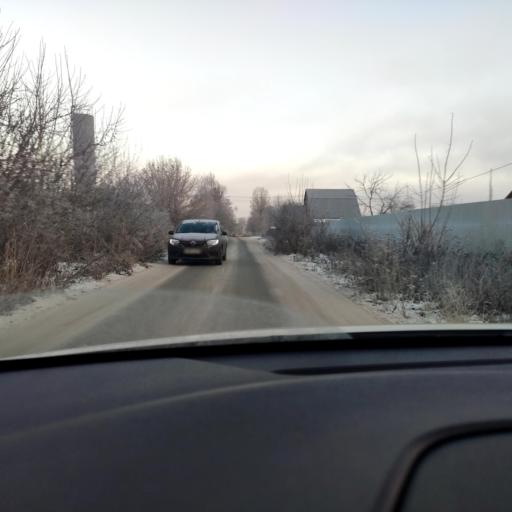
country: RU
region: Tatarstan
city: Staroye Arakchino
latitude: 55.8630
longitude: 49.0468
